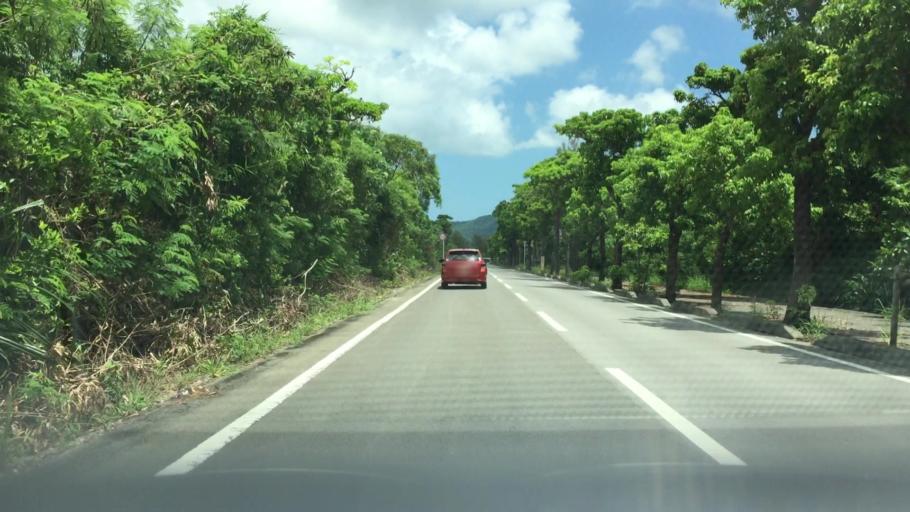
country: JP
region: Okinawa
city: Ishigaki
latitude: 24.3977
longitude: 124.1409
